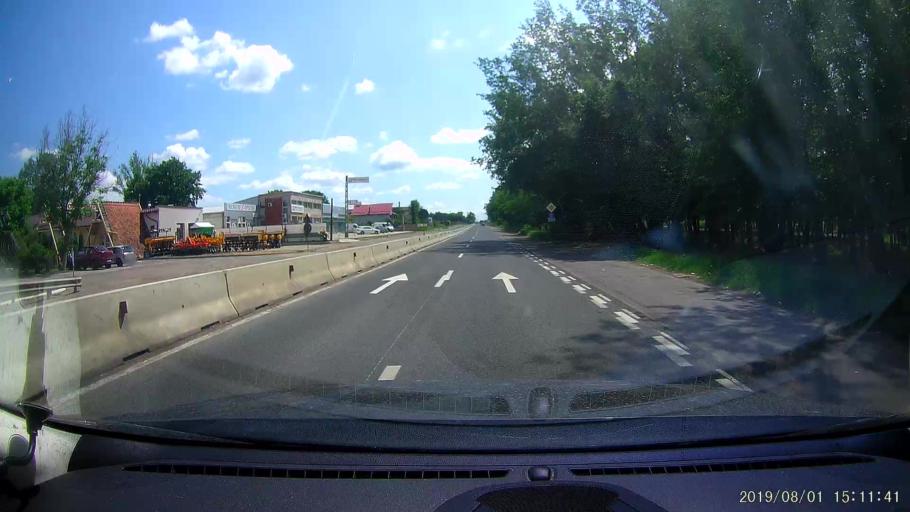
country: RO
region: Braila
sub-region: Comuna Chiscani
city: Chiscani
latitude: 45.2155
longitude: 27.9221
